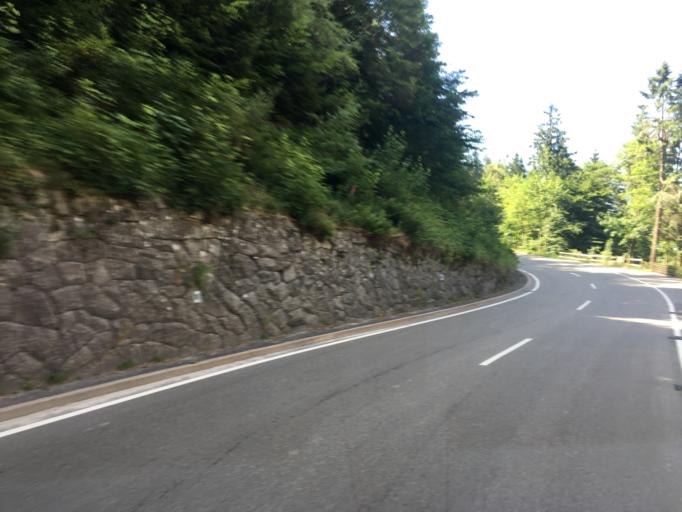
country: DE
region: Baden-Wuerttemberg
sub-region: Freiburg Region
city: Seebach
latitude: 48.5856
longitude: 8.2062
